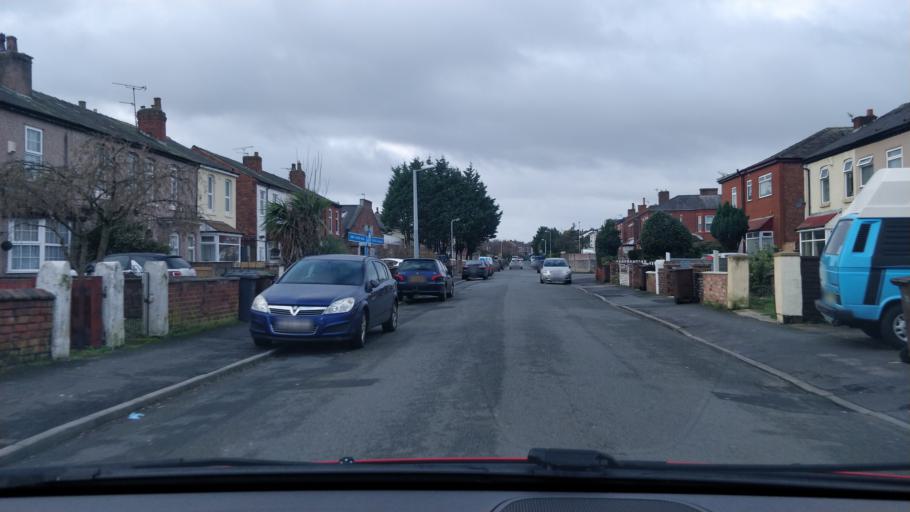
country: GB
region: England
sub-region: Sefton
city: Southport
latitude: 53.6301
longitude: -3.0051
